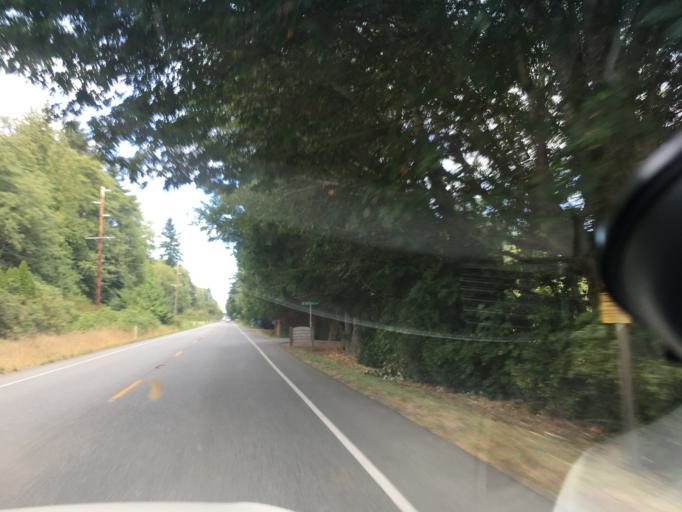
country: US
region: Washington
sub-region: Kitsap County
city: Lofall
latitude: 47.8199
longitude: -122.5848
